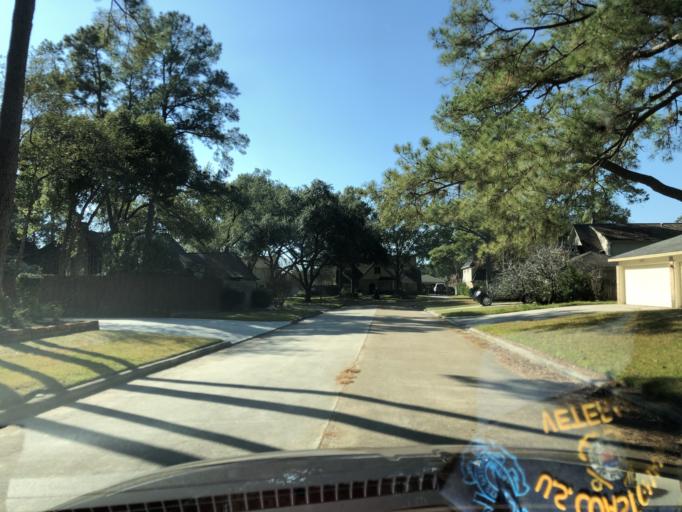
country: US
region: Texas
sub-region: Harris County
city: Tomball
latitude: 30.0260
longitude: -95.5525
